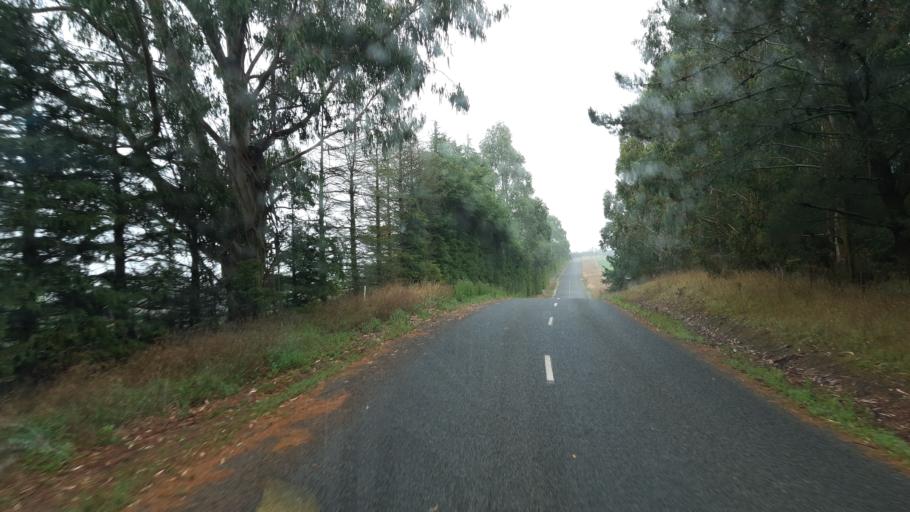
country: NZ
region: Otago
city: Oamaru
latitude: -44.9394
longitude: 170.7320
